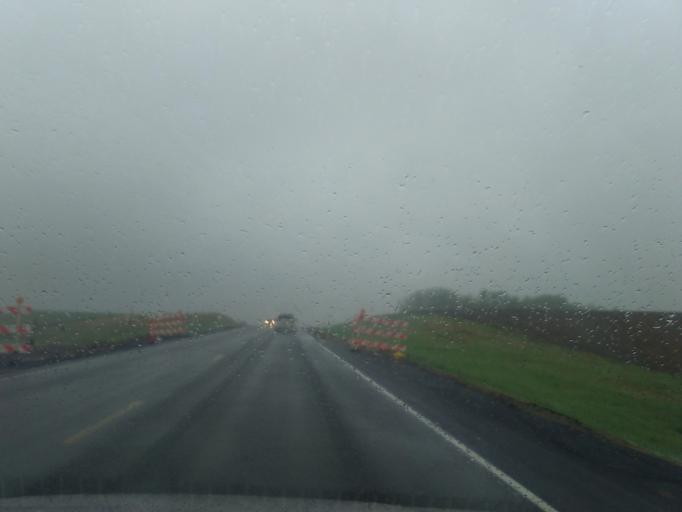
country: US
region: Nebraska
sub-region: Wayne County
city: Wayne
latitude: 42.1875
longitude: -97.1772
